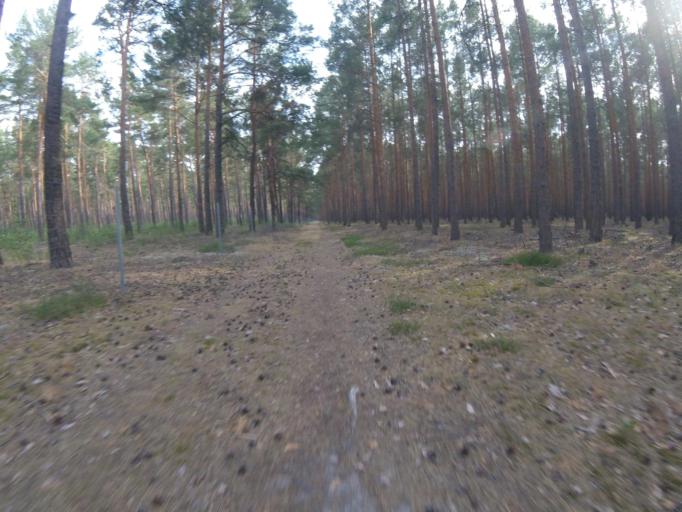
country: DE
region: Brandenburg
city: Bestensee
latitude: 52.2385
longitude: 13.7567
